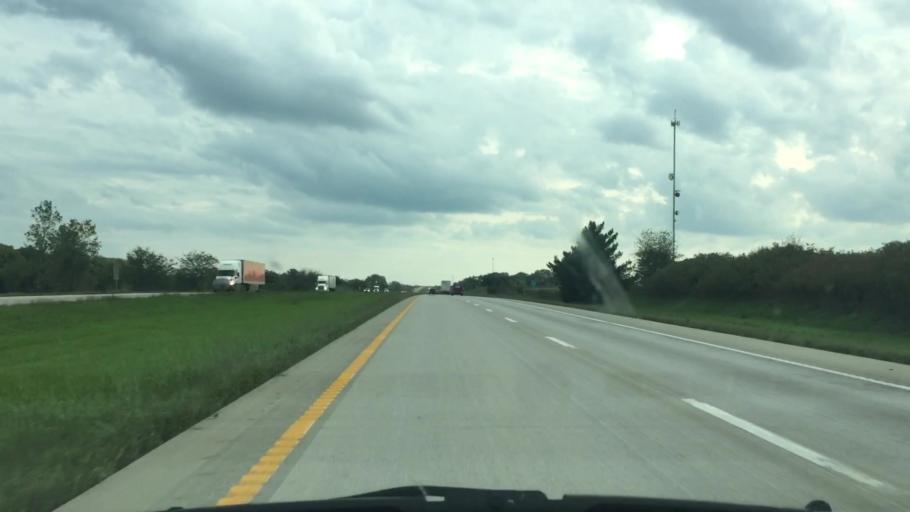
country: US
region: Missouri
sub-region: Clinton County
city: Lathrop
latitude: 39.6143
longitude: -94.2497
